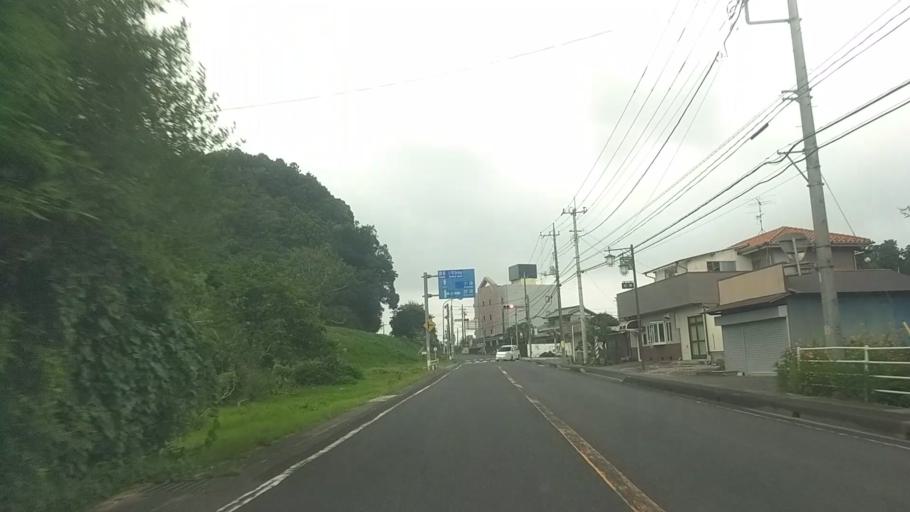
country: JP
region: Chiba
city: Ohara
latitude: 35.2824
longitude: 140.2873
